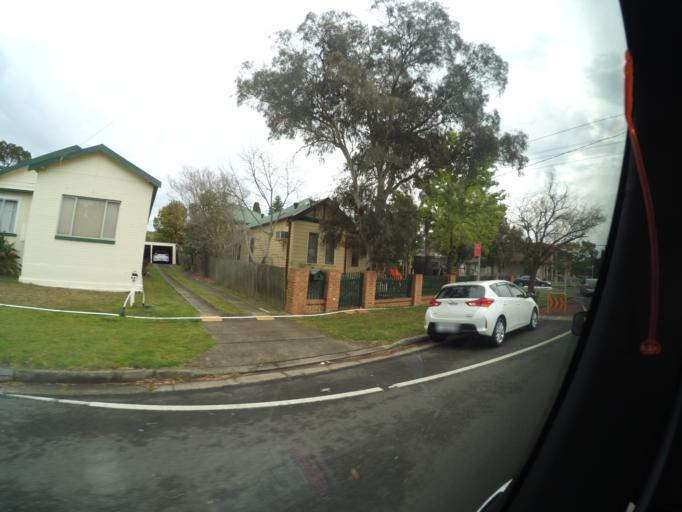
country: AU
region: New South Wales
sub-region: Bankstown
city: Bankstown
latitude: -33.9237
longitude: 151.0252
